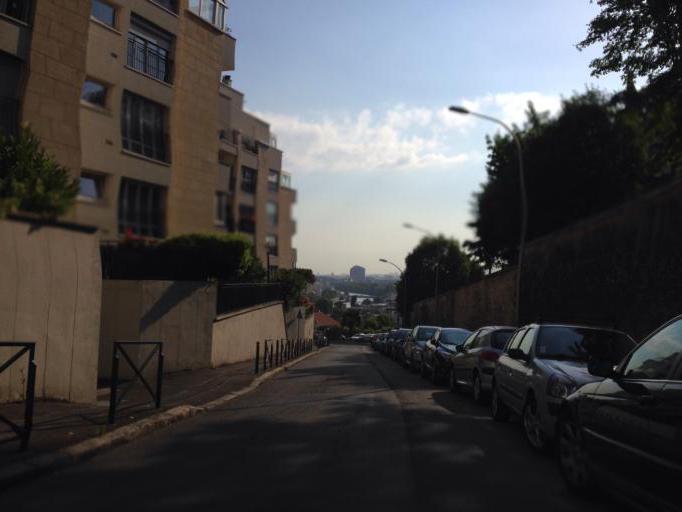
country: FR
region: Ile-de-France
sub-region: Departement des Hauts-de-Seine
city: Meudon
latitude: 48.8184
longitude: 2.2336
